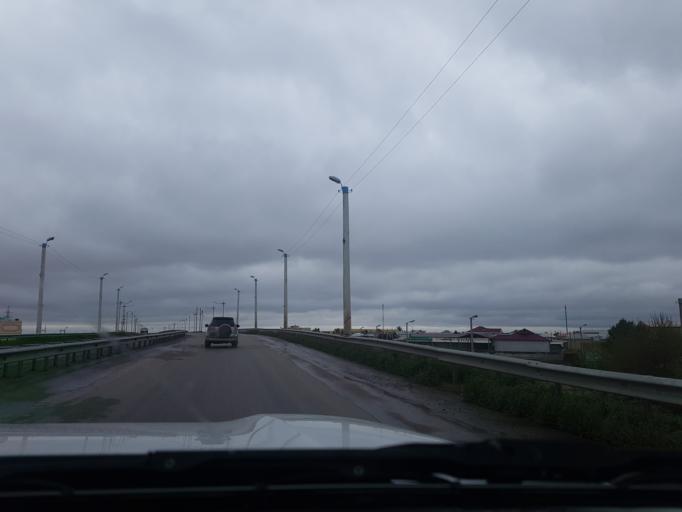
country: TM
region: Mary
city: Mary
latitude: 37.5902
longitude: 61.8837
